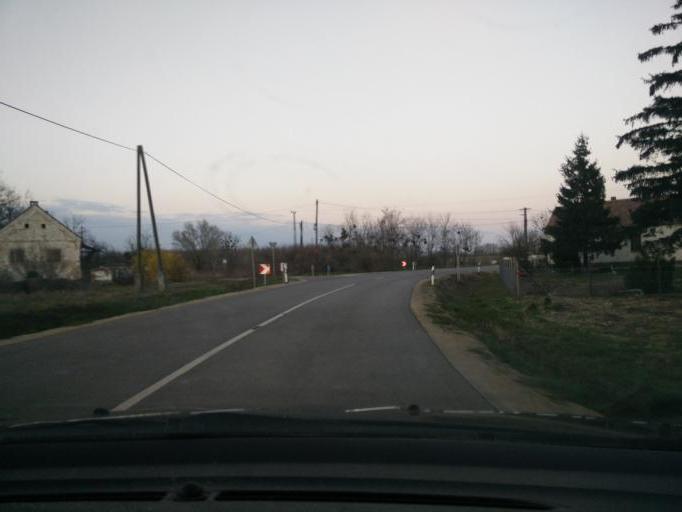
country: HU
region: Veszprem
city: Csabrendek
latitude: 47.0693
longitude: 17.3528
